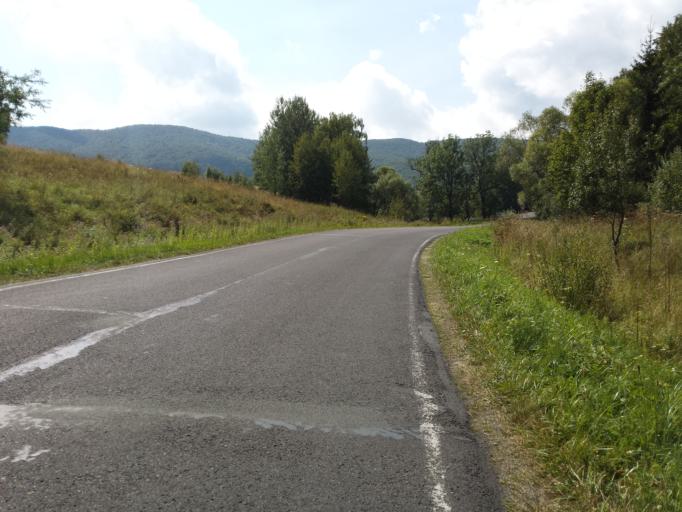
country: PL
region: Subcarpathian Voivodeship
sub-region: Powiat bieszczadzki
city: Lutowiska
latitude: 49.1406
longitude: 22.5611
